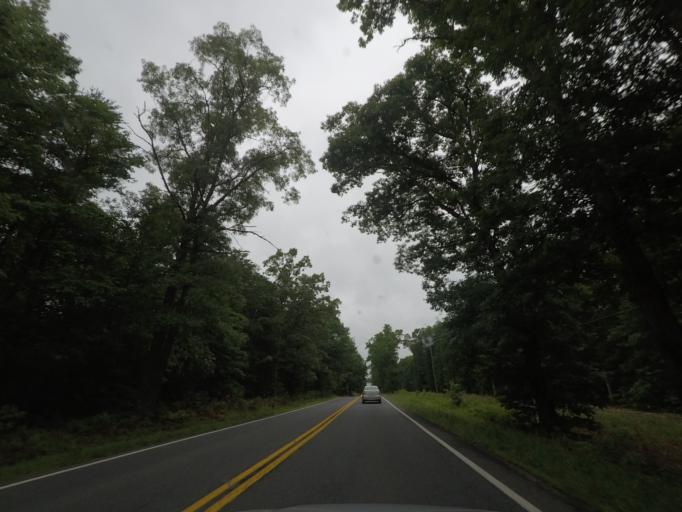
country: US
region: Virginia
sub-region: Fluvanna County
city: Palmyra
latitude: 37.9533
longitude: -78.2350
